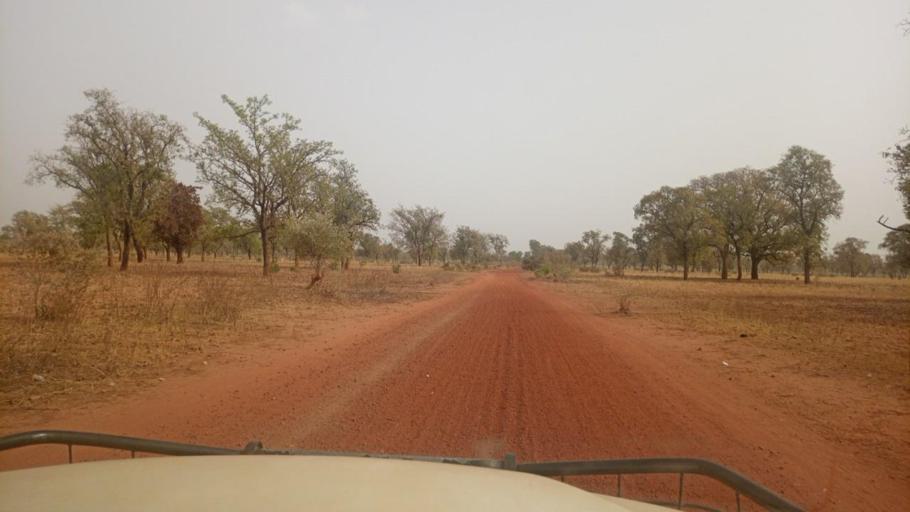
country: BF
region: Boucle du Mouhoun
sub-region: Province des Banwa
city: Salanso
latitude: 12.1028
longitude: -4.3344
